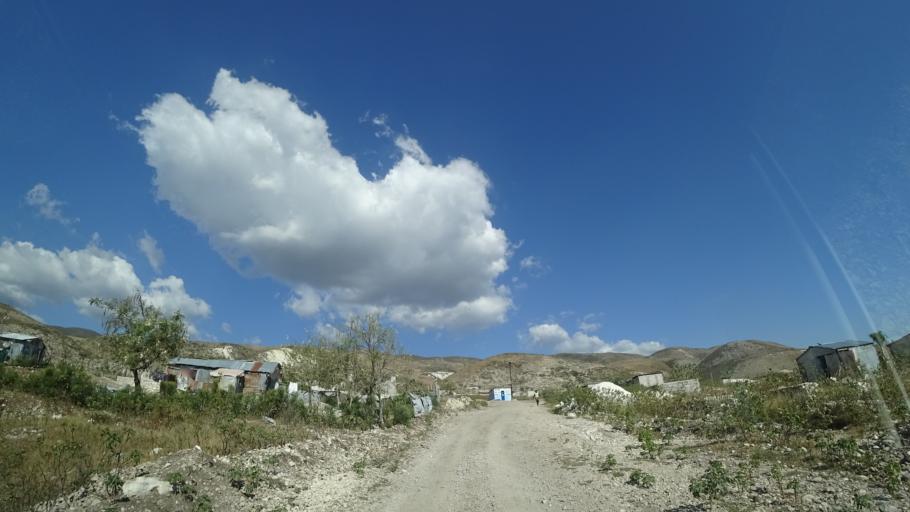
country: HT
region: Ouest
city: Cabaret
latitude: 18.6887
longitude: -72.3121
